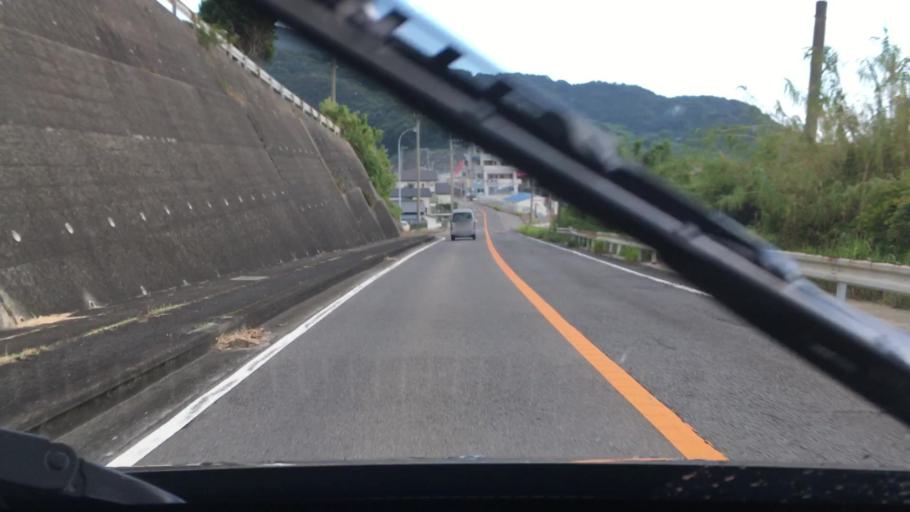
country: JP
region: Nagasaki
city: Togitsu
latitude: 32.8830
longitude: 129.6788
